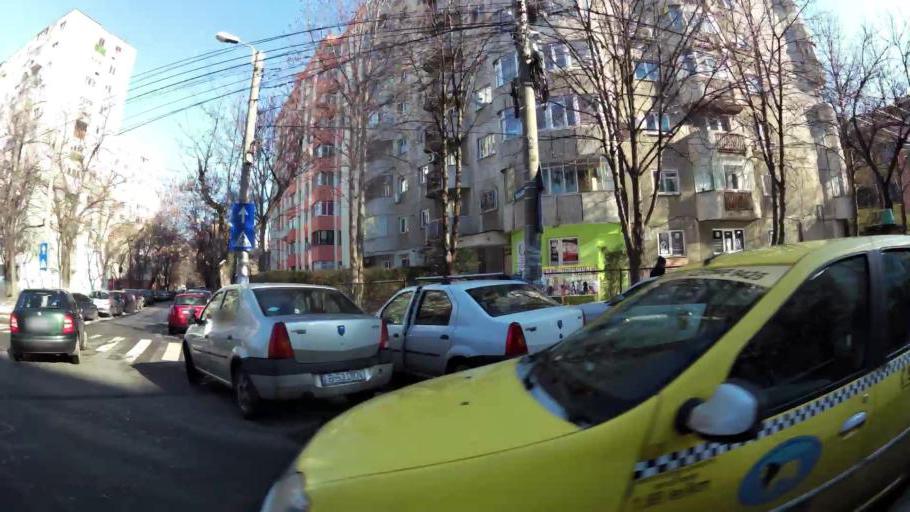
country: RO
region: Bucuresti
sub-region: Municipiul Bucuresti
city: Bucharest
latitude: 44.4619
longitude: 26.1265
